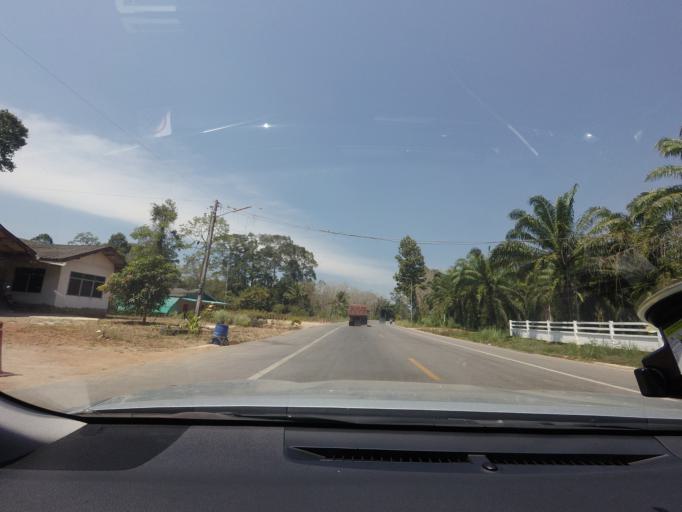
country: TH
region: Surat Thani
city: Tha Chang
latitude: 9.2592
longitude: 99.1858
